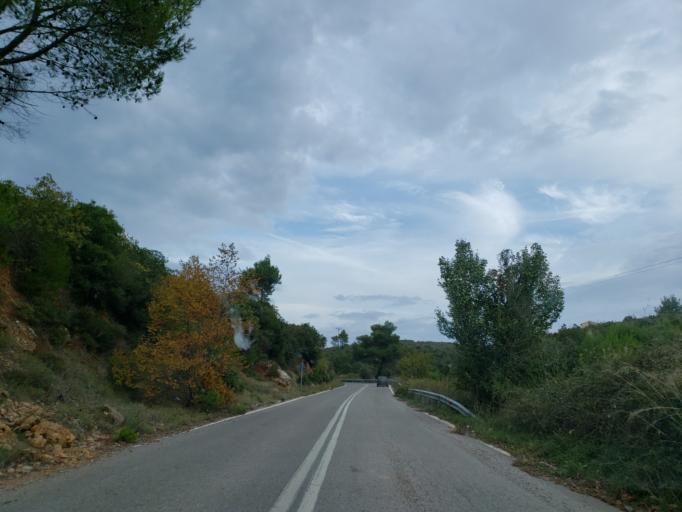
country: GR
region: Attica
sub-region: Nomarchia Anatolikis Attikis
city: Varnavas
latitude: 38.2196
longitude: 23.9319
